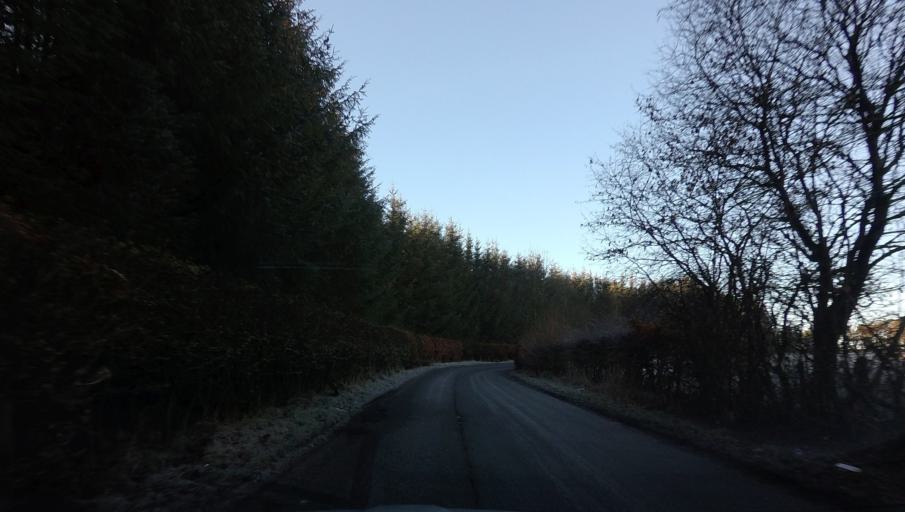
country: GB
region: Scotland
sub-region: North Lanarkshire
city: Newmains
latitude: 55.8063
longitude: -3.8572
